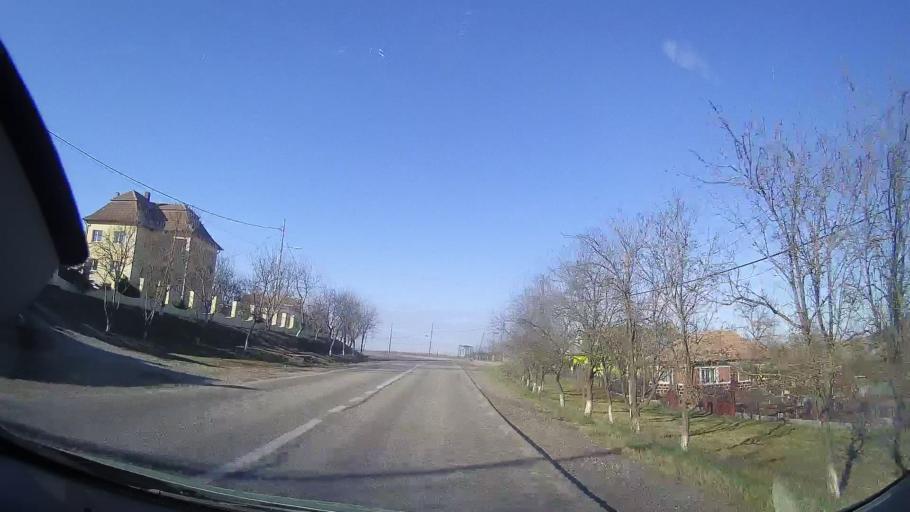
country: RO
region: Cluj
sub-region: Comuna Mociu
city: Mociu
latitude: 46.7916
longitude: 24.0715
